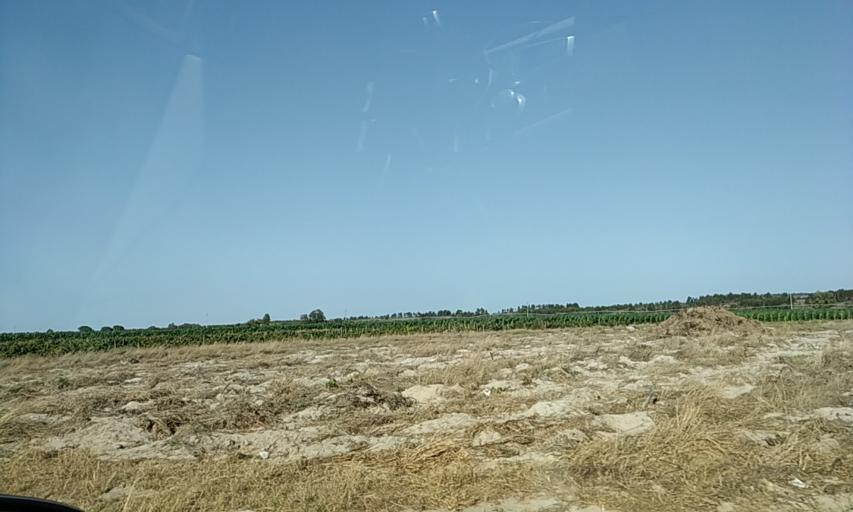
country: PT
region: Santarem
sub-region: Almeirim
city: Almeirim
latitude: 39.1560
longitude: -8.6203
